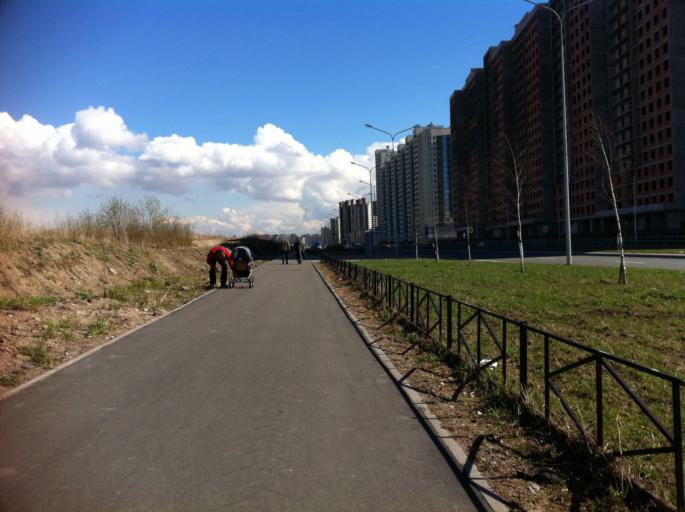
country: RU
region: St.-Petersburg
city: Uritsk
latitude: 59.8679
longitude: 30.1729
